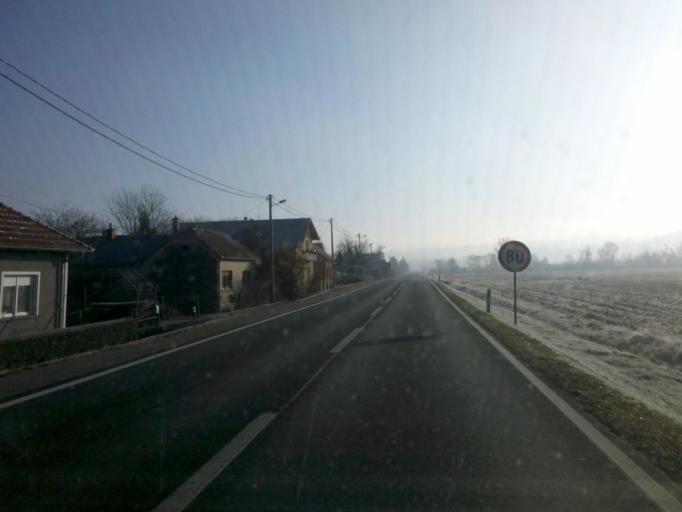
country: HR
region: Koprivnicko-Krizevacka
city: Reka
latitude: 46.1981
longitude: 16.7194
